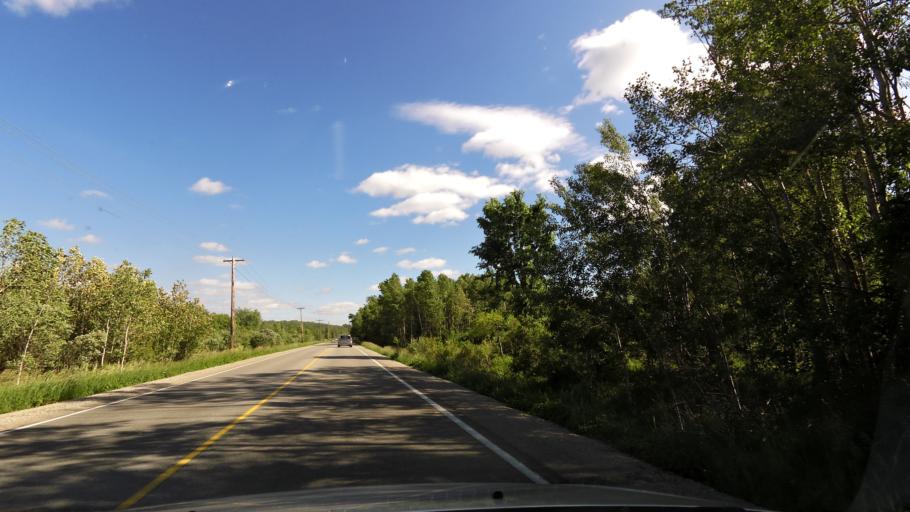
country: CA
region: Ontario
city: Innisfil
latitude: 44.2115
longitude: -79.6292
